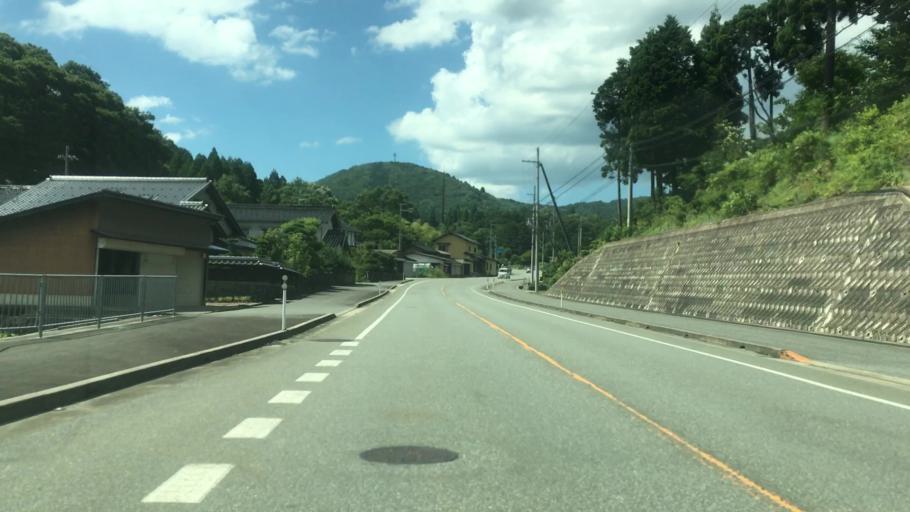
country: JP
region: Hyogo
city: Toyooka
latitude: 35.4815
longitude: 134.7080
